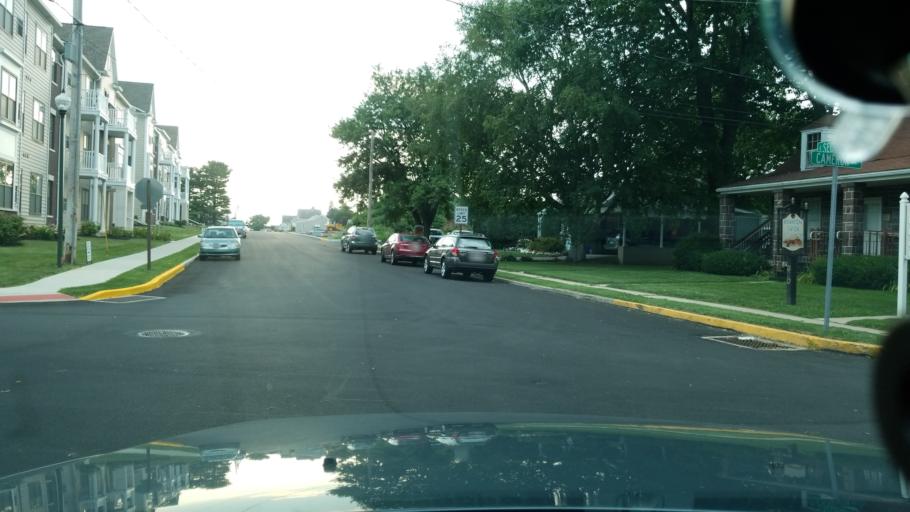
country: US
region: Pennsylvania
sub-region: Dauphin County
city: Hummelstown
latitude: 40.2671
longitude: -76.6983
